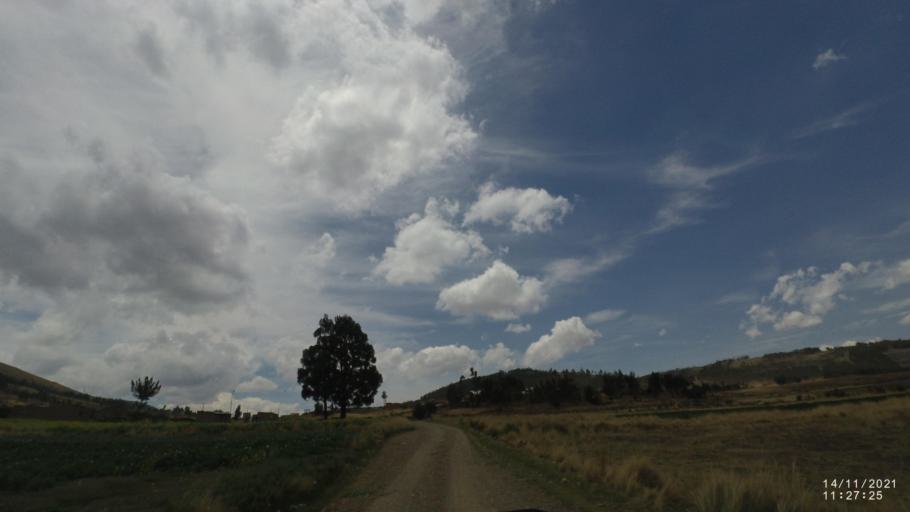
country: BO
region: Cochabamba
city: Colomi
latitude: -17.3404
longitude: -66.0149
